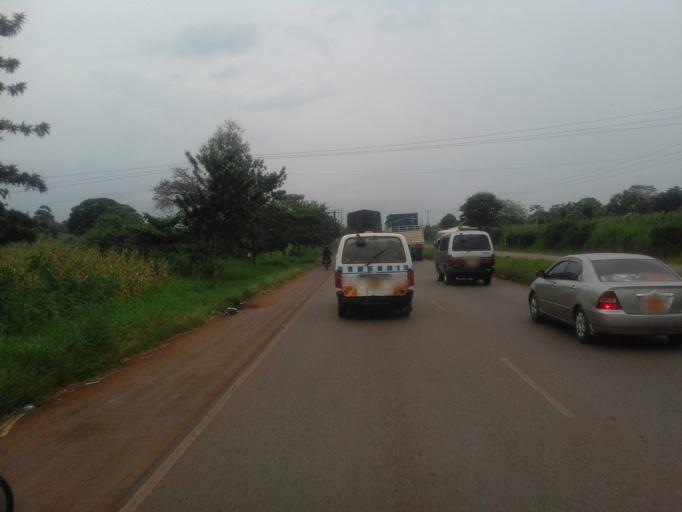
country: UG
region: Eastern Region
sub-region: Jinja District
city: Jinja
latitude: 0.4455
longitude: 33.2043
